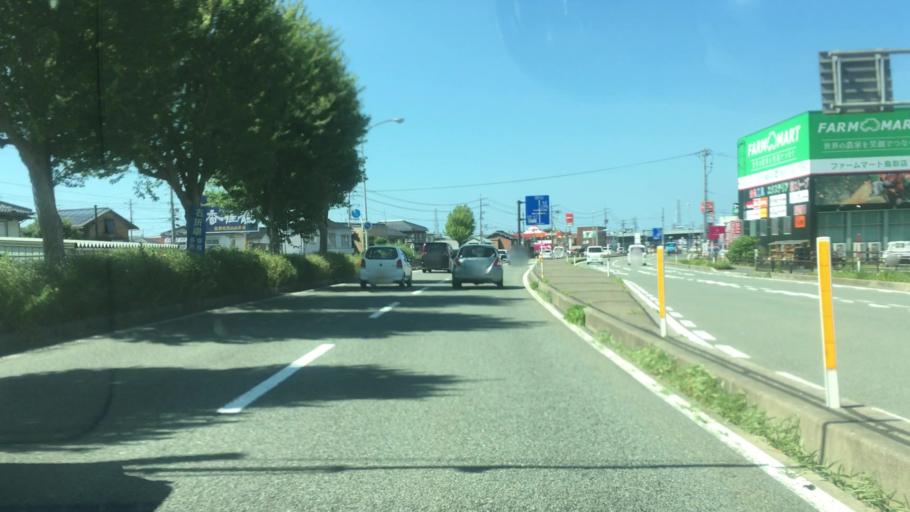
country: JP
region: Tottori
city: Tottori
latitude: 35.4746
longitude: 134.2168
